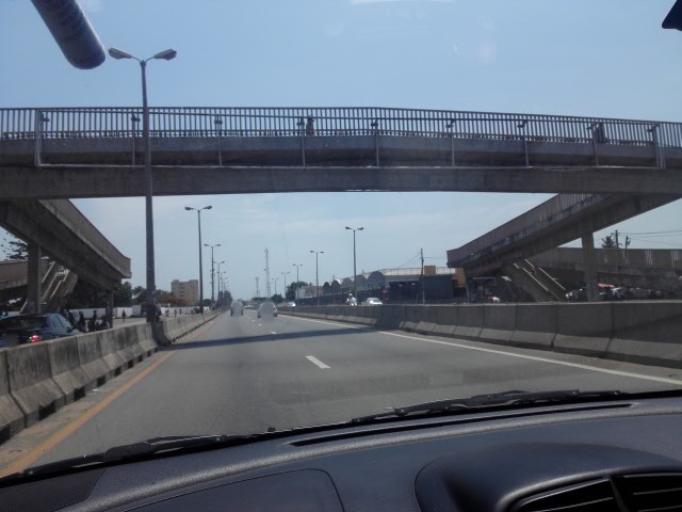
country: MZ
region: Maputo City
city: Maputo
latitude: -25.9395
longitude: 32.5457
